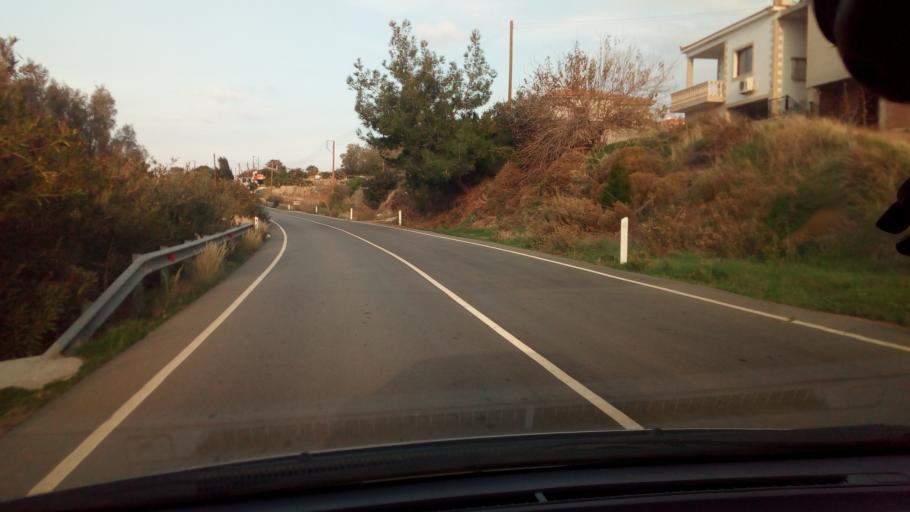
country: CY
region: Lefkosia
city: Kato Pyrgos
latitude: 35.1496
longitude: 32.5378
